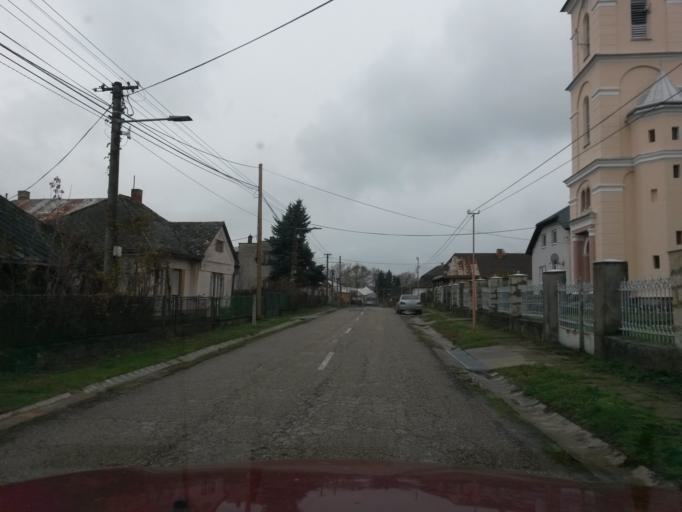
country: SK
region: Kosicky
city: Cierna nad Tisou
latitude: 48.5573
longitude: 21.9561
